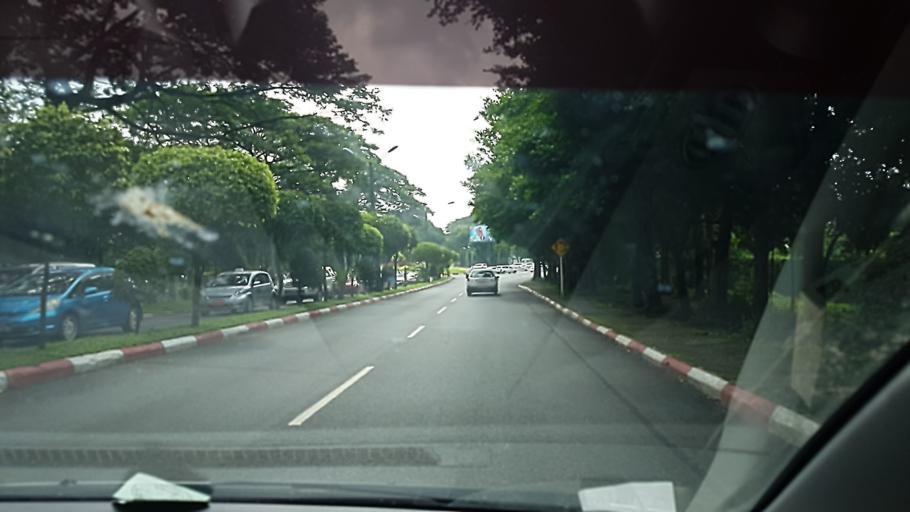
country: MM
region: Yangon
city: Yangon
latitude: 16.7958
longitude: 96.1551
